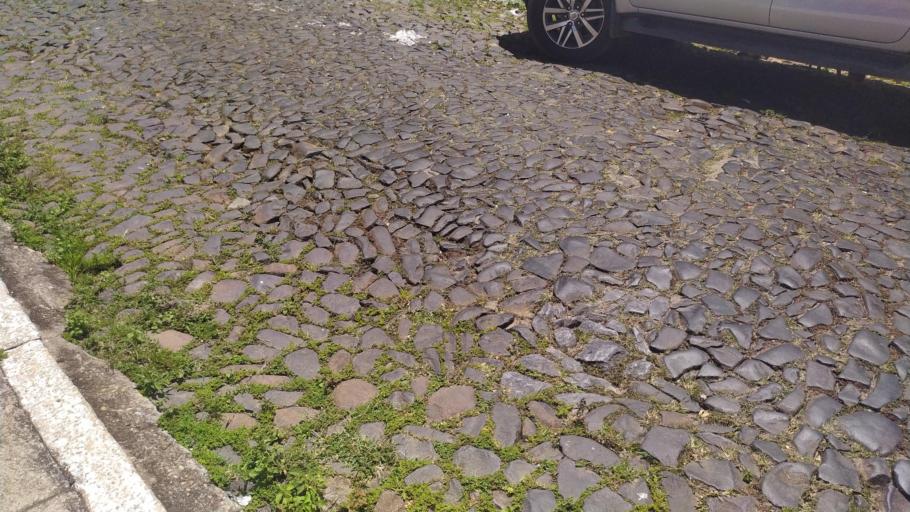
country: BR
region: Minas Gerais
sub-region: Sao Joao Del Rei
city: Sao Joao del Rei
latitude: -21.1341
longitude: -44.2634
